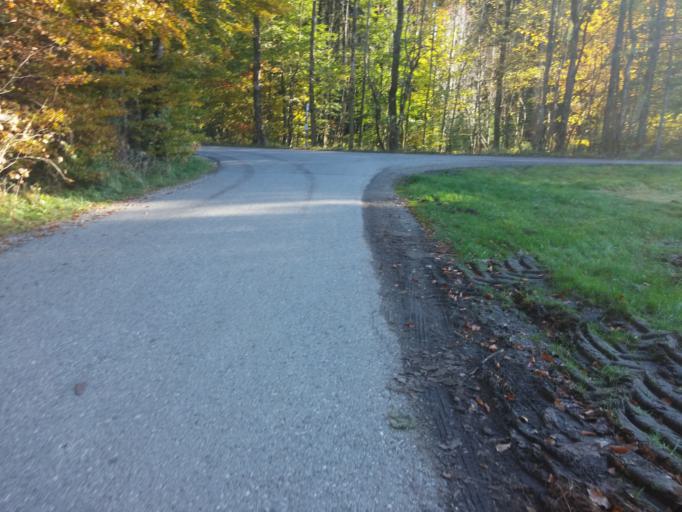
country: DE
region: Bavaria
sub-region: Upper Bavaria
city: Aying
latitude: 47.9630
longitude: 11.7896
